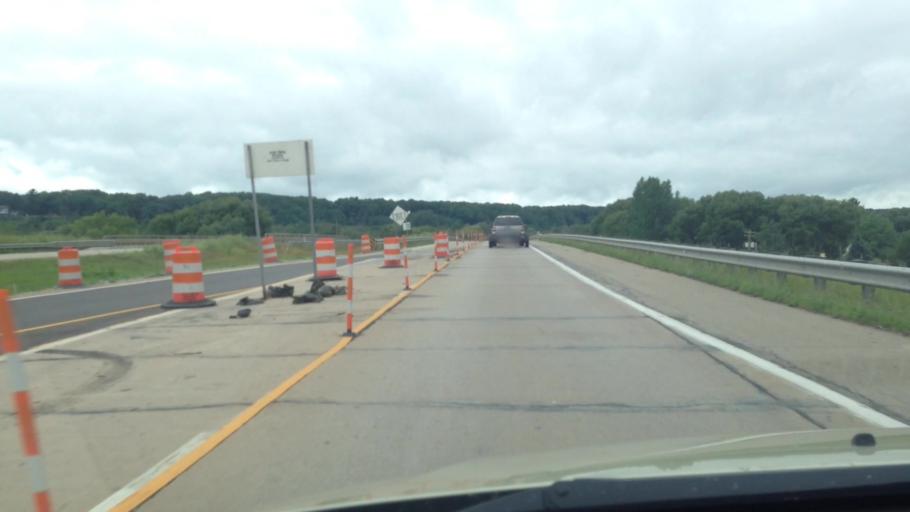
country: US
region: Michigan
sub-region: Delta County
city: Gladstone
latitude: 45.8587
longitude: -87.0250
